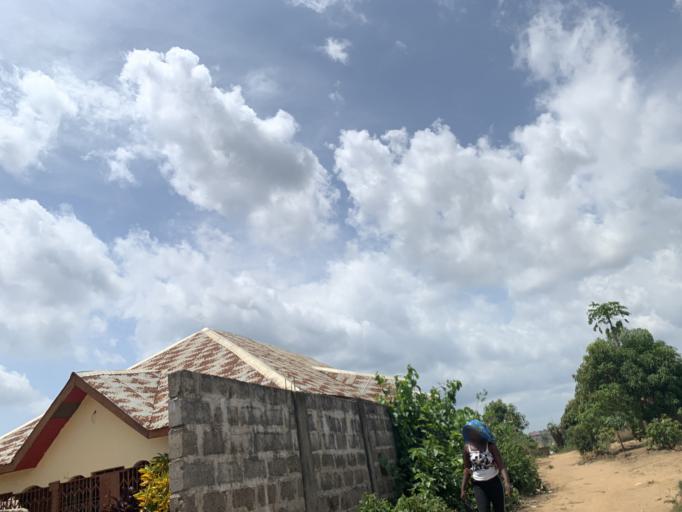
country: SL
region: Western Area
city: Waterloo
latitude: 8.3411
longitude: -13.0258
